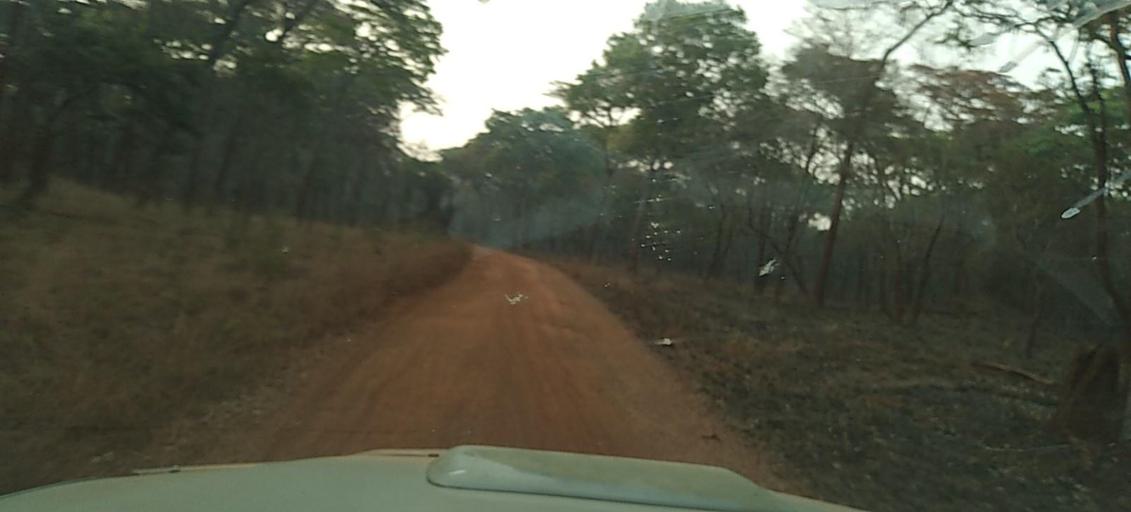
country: ZM
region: North-Western
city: Kasempa
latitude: -13.0934
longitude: 26.4008
